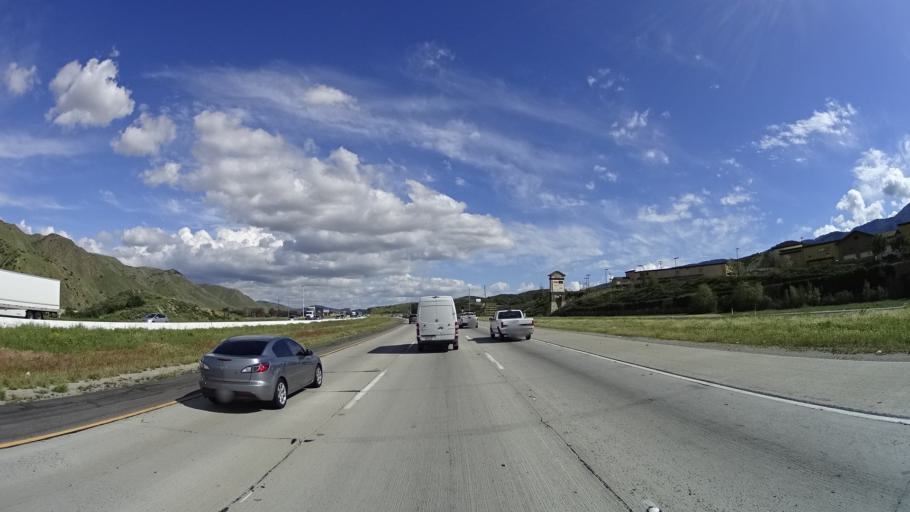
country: US
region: California
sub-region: Riverside County
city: El Cerrito
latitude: 33.7482
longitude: -117.4522
